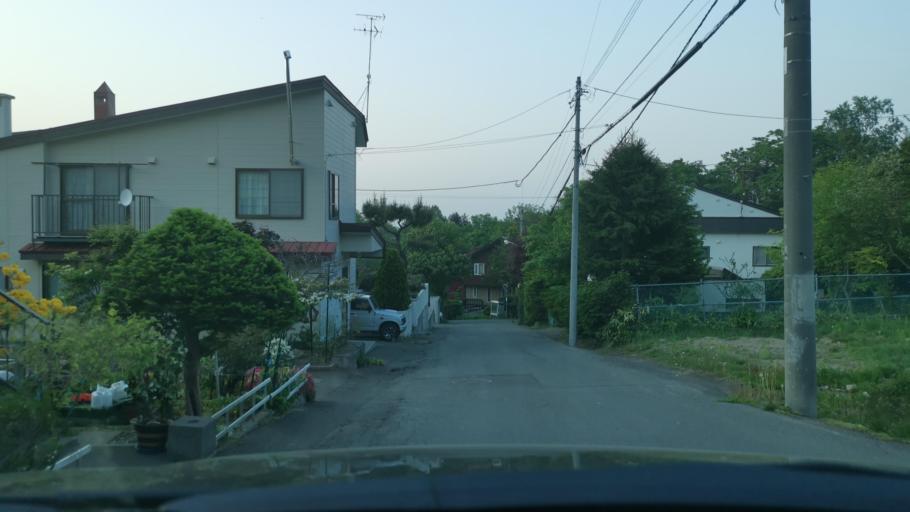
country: JP
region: Hokkaido
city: Sapporo
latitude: 43.0362
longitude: 141.3165
